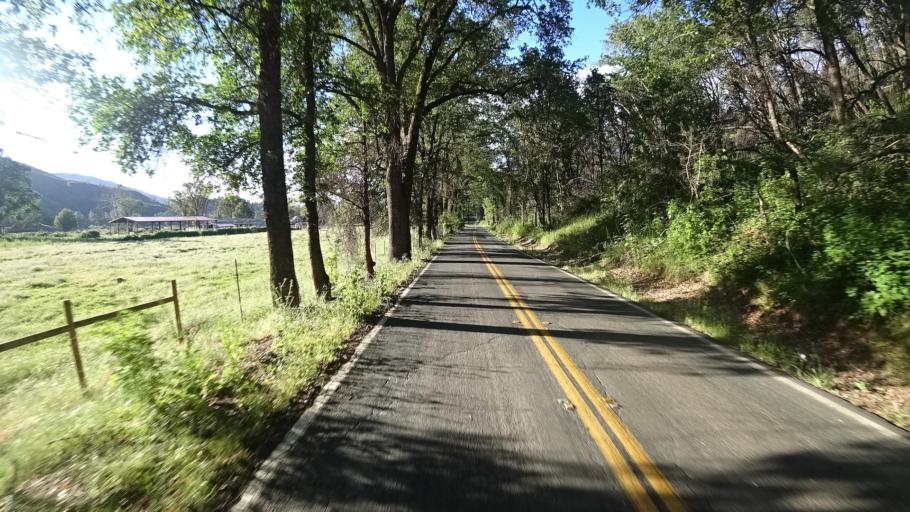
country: US
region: California
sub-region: Lake County
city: Upper Lake
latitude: 39.2162
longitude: -122.9339
